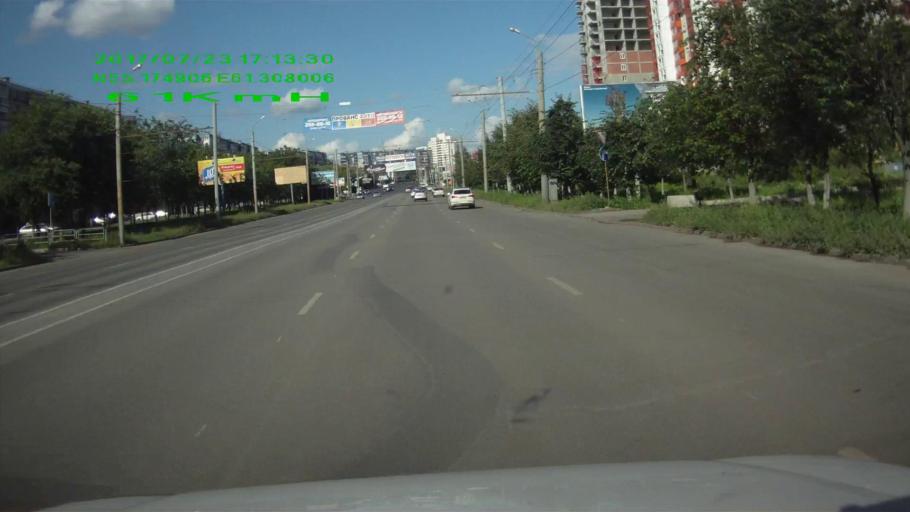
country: RU
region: Chelyabinsk
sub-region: Gorod Chelyabinsk
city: Chelyabinsk
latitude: 55.1752
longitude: 61.3087
